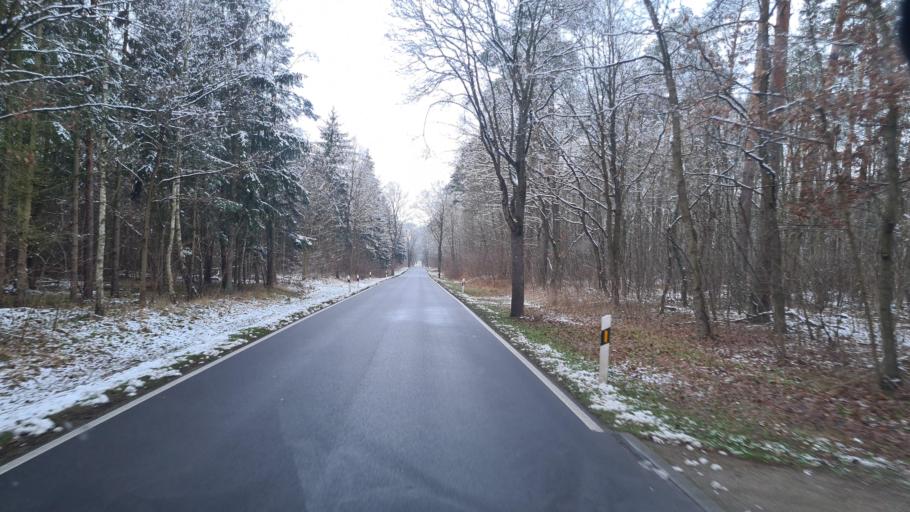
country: DE
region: Brandenburg
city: Strausberg
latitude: 52.5523
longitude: 13.9162
